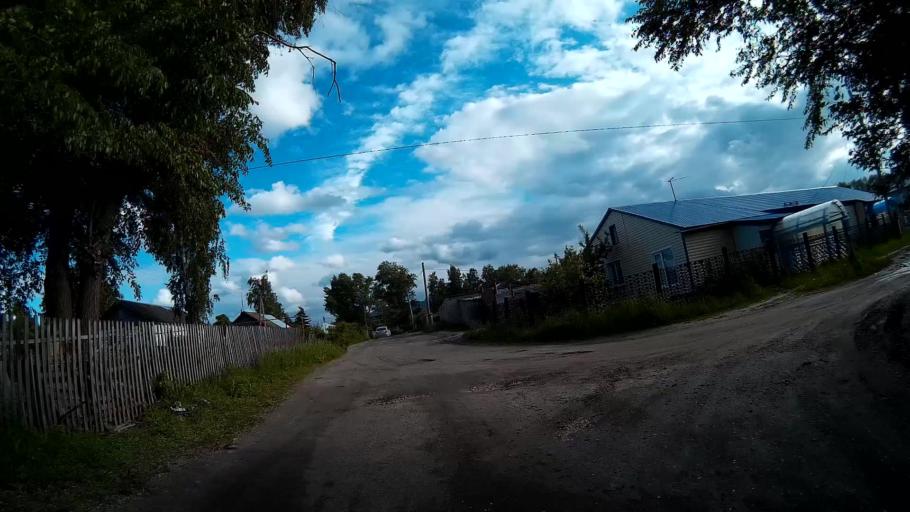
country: RU
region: Ulyanovsk
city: Novoul'yanovsk
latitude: 54.2060
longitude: 48.2659
